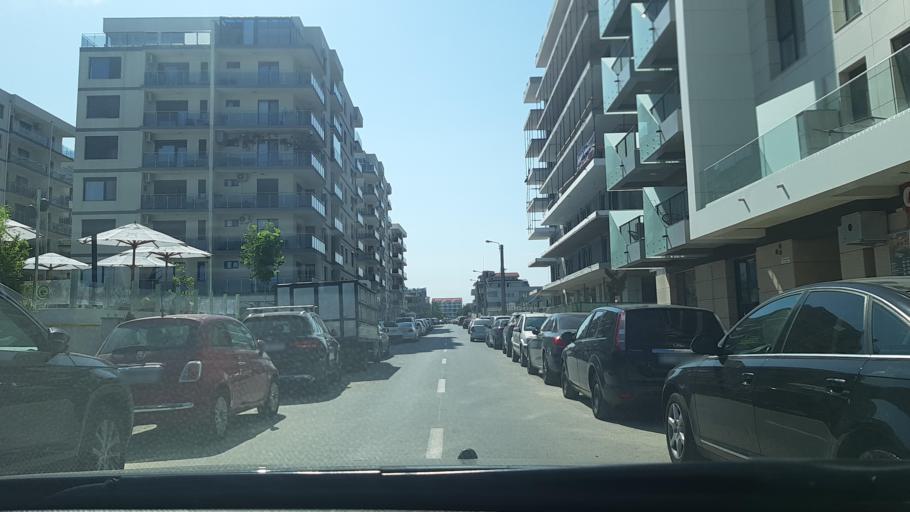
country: RO
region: Constanta
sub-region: Comuna Navodari
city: Navodari
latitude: 44.3047
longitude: 28.6279
